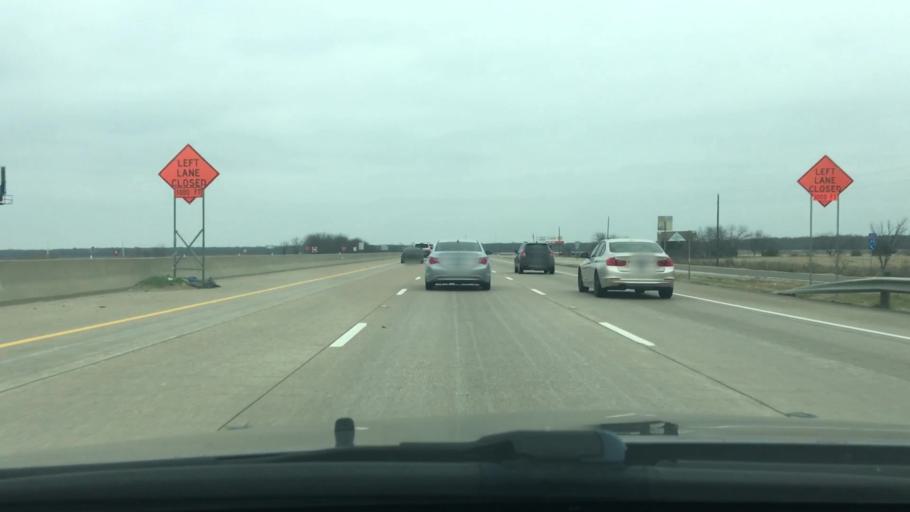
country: US
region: Texas
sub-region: Navarro County
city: Corsicana
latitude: 32.1790
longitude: -96.4713
